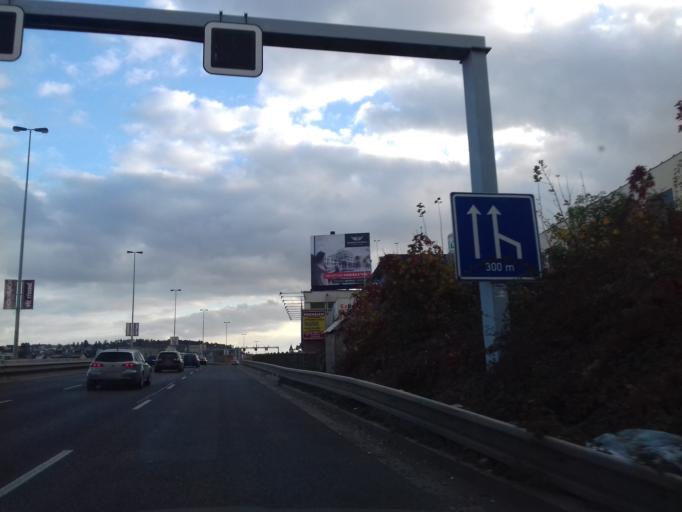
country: CZ
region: Praha
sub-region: Praha 2
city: Vysehrad
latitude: 50.0553
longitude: 14.4071
